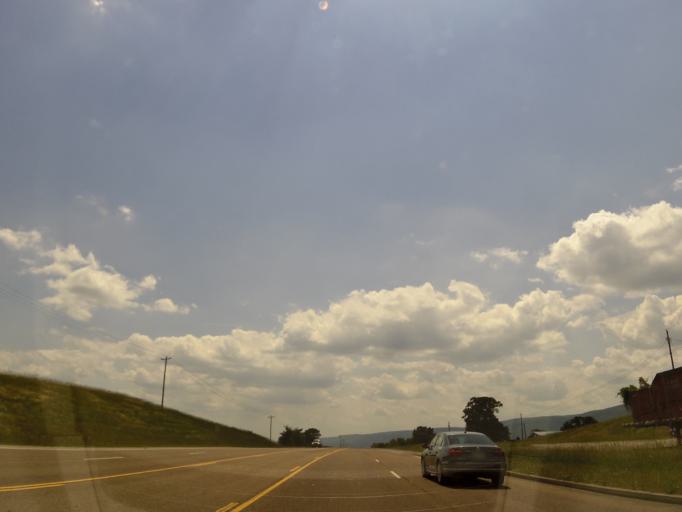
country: US
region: Tennessee
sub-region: Bledsoe County
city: Pikeville
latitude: 35.5939
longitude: -85.1989
